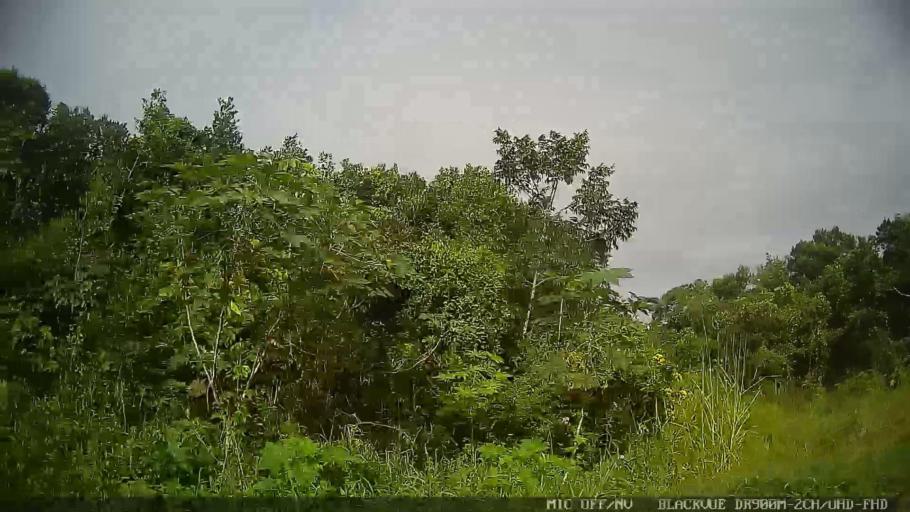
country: BR
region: Sao Paulo
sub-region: Peruibe
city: Peruibe
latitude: -24.2320
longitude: -46.9172
